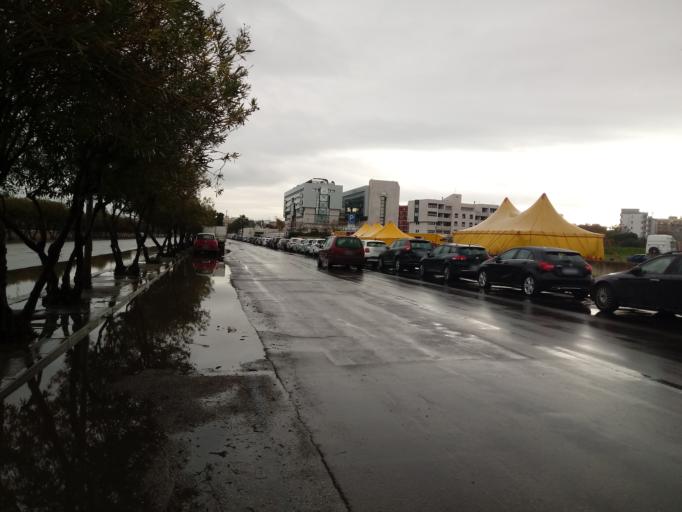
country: IT
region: Apulia
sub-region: Provincia di Bari
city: Bari
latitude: 41.1318
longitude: 16.8470
